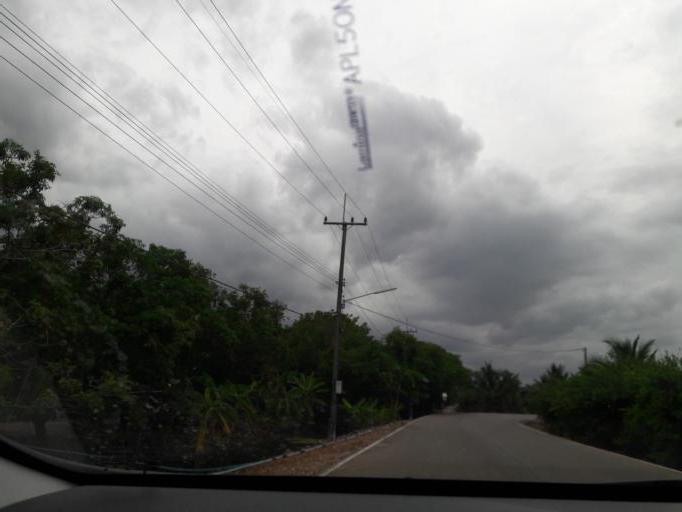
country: TH
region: Ratchaburi
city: Damnoen Saduak
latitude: 13.5611
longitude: 99.9869
